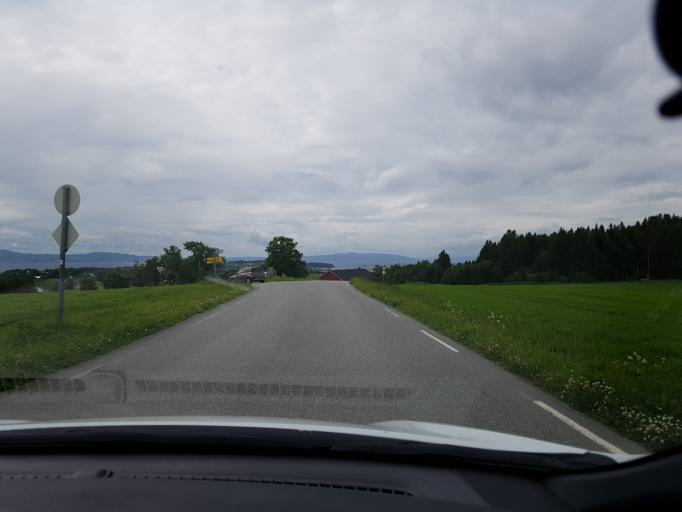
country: NO
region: Nord-Trondelag
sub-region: Frosta
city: Frosta
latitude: 63.5792
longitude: 10.7139
